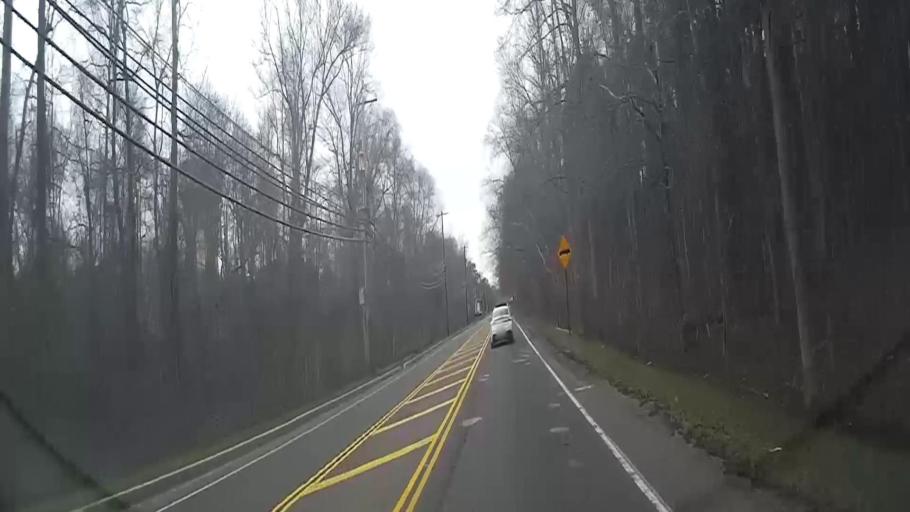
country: US
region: New Jersey
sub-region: Burlington County
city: Marlton
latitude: 39.8574
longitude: -74.8675
